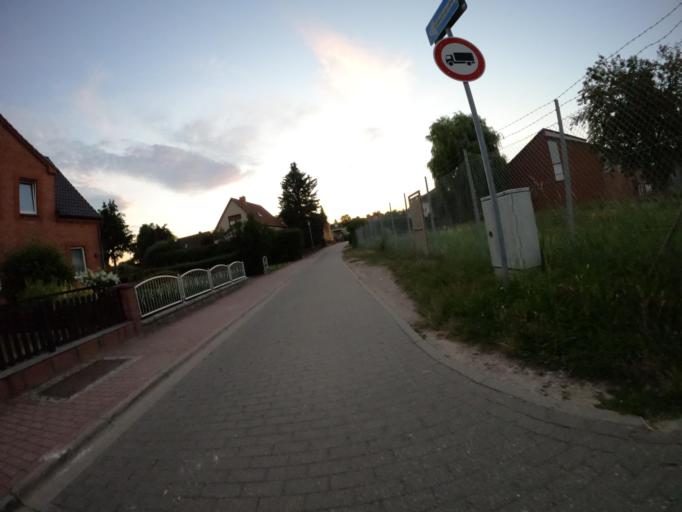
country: DE
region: Mecklenburg-Vorpommern
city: Woldegk
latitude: 53.4596
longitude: 13.5781
